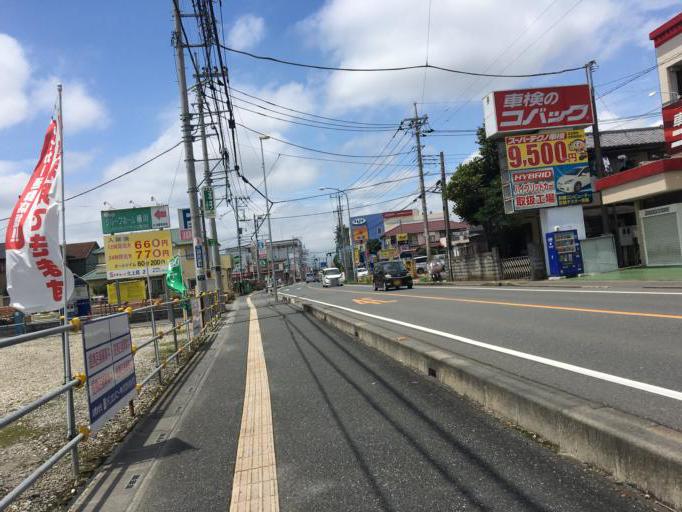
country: JP
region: Saitama
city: Okegawa
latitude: 35.9856
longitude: 139.5794
